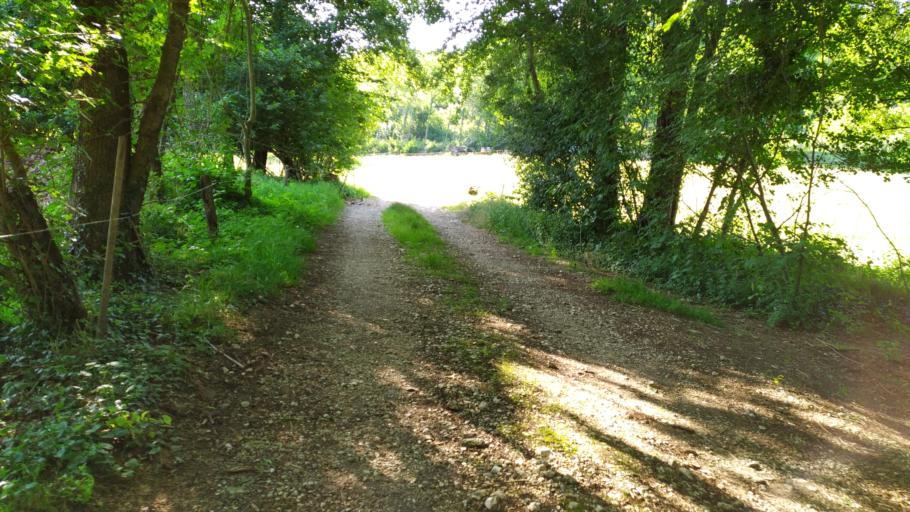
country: IT
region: Veneto
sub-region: Provincia di Vicenza
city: Monte di Malo
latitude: 45.6851
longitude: 11.3605
